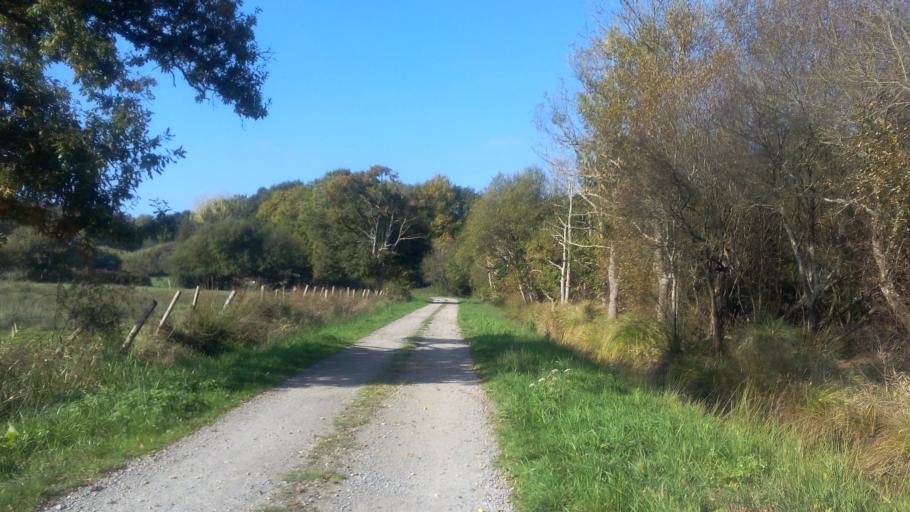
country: FR
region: Brittany
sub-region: Departement du Morbihan
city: Saint-Jean-la-Poterie
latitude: 47.6514
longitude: -2.1182
